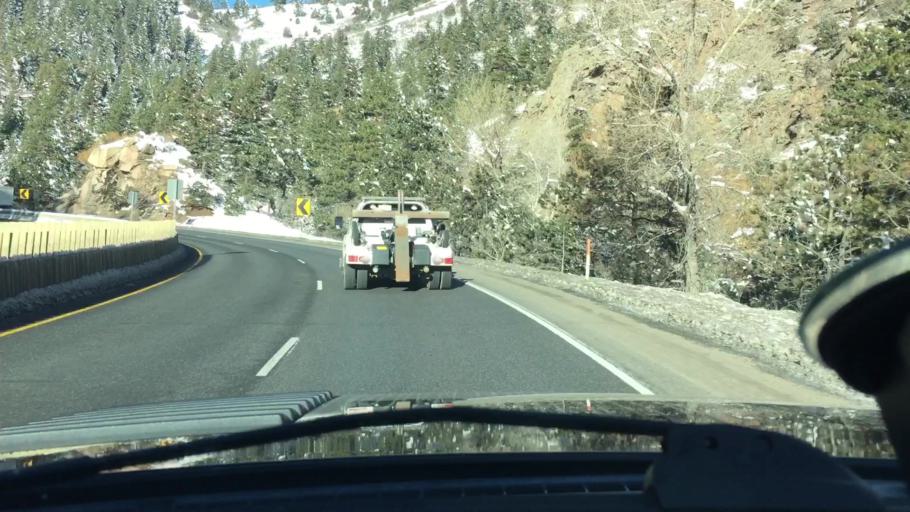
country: US
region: Colorado
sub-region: Jefferson County
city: Indian Hills
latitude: 39.6196
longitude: -105.2263
